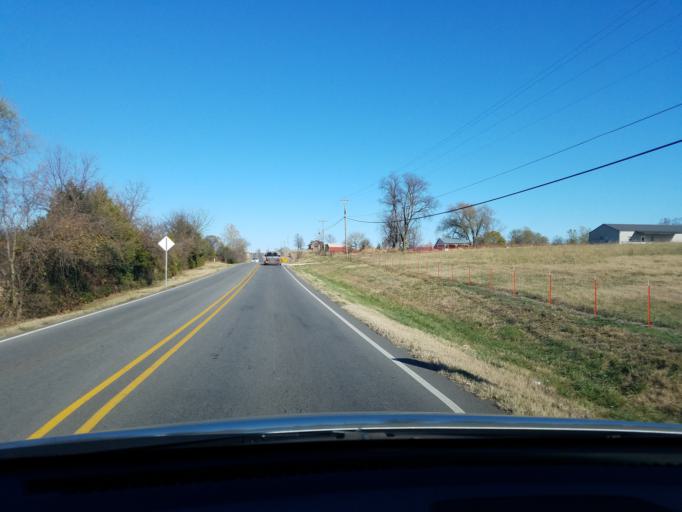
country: US
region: Arkansas
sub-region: Carroll County
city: Berryville
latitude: 36.3874
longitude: -93.5663
